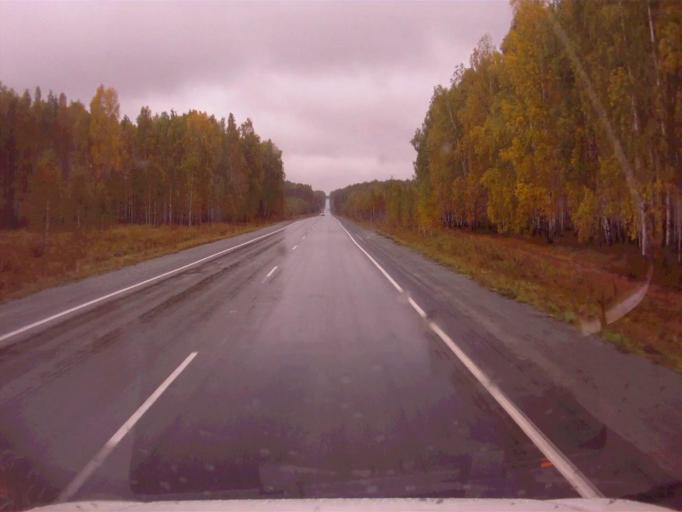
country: RU
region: Chelyabinsk
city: Tayginka
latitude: 55.5130
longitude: 60.6393
